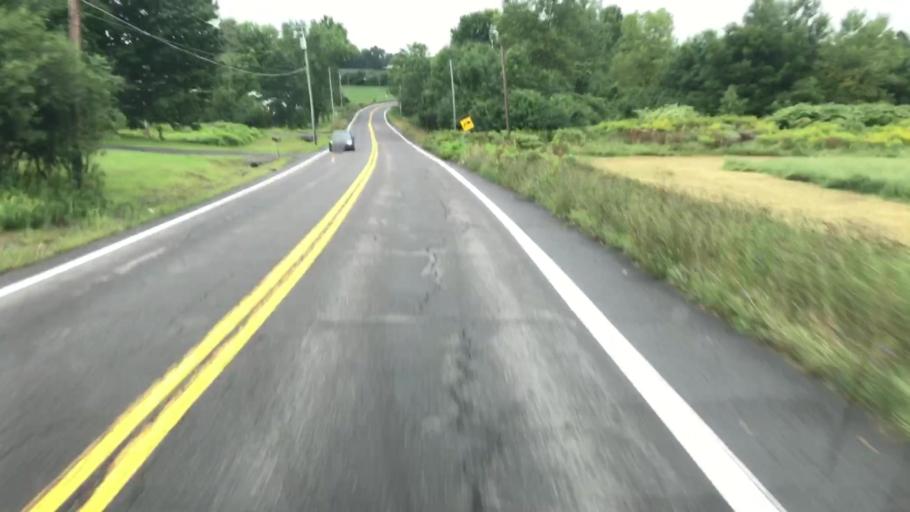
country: US
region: New York
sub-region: Onondaga County
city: Skaneateles
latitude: 42.9598
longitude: -76.4443
